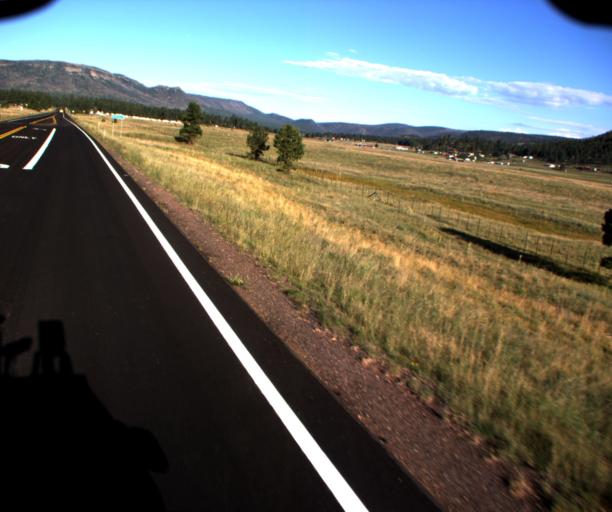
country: US
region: Arizona
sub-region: Apache County
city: Eagar
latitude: 33.8275
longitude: -109.0975
